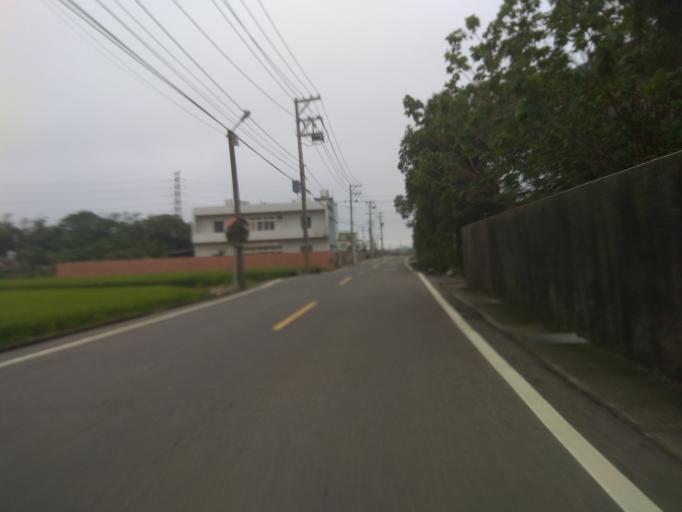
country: TW
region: Taiwan
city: Taoyuan City
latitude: 24.9976
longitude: 121.1231
